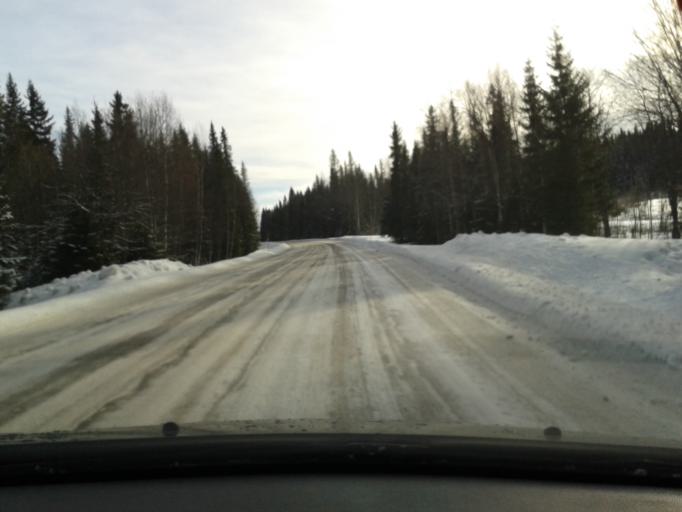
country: SE
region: Vaesterbotten
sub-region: Vilhelmina Kommun
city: Sjoberg
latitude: 64.7390
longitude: 16.2077
